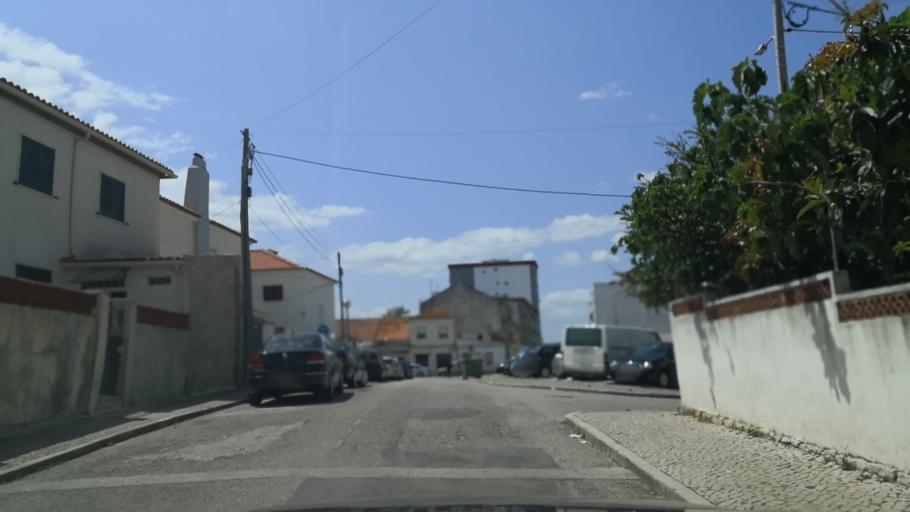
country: PT
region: Setubal
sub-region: Setubal
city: Setubal
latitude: 38.5256
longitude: -8.8784
